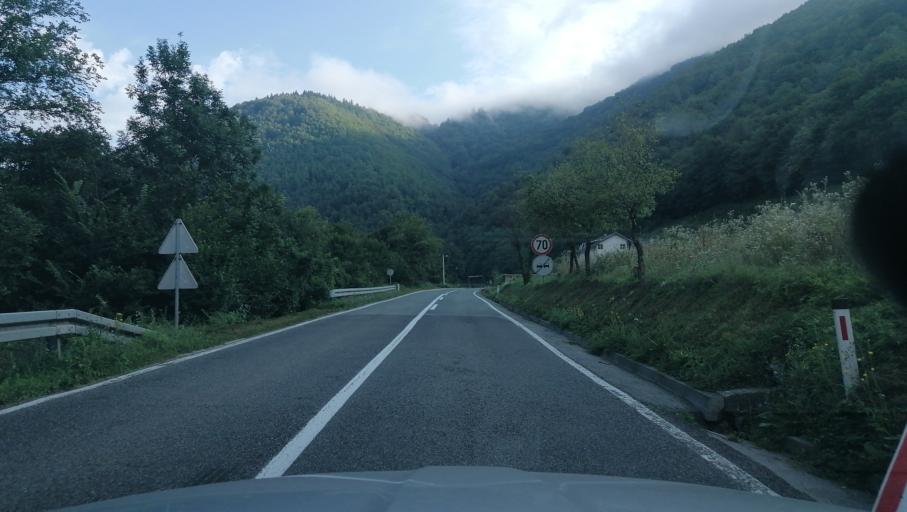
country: BA
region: Federation of Bosnia and Herzegovina
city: Jajce
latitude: 44.2325
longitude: 17.3033
